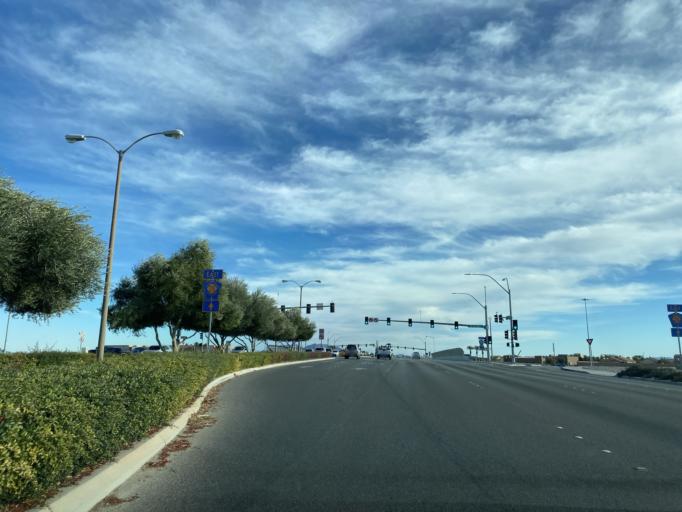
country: US
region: Nevada
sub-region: Clark County
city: North Las Vegas
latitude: 36.2908
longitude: -115.1817
